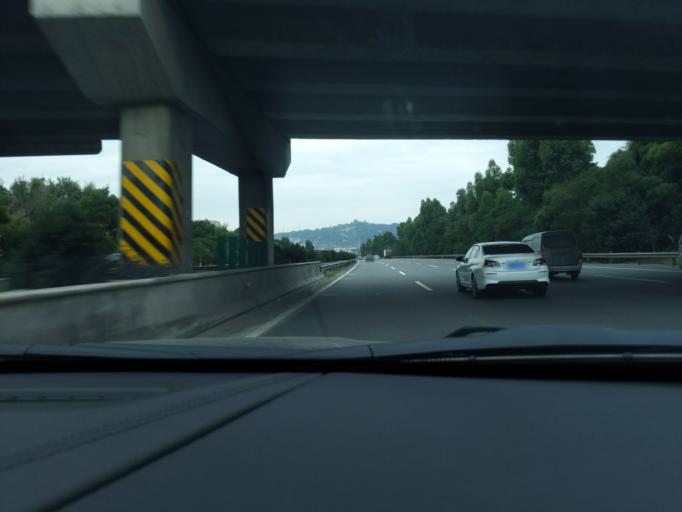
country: CN
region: Fujian
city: Xike
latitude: 24.6728
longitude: 118.1245
